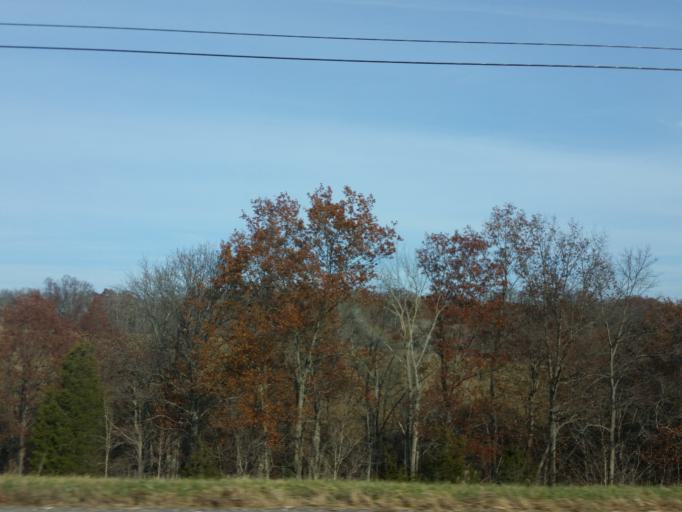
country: US
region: Kentucky
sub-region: Pendleton County
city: Falmouth
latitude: 38.5783
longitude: -84.3006
